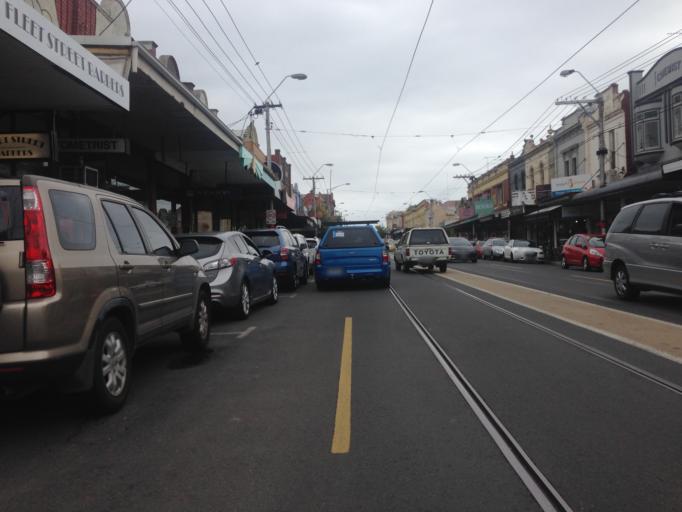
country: AU
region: Victoria
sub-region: Darebin
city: Northcote
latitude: -37.7721
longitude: 144.9985
